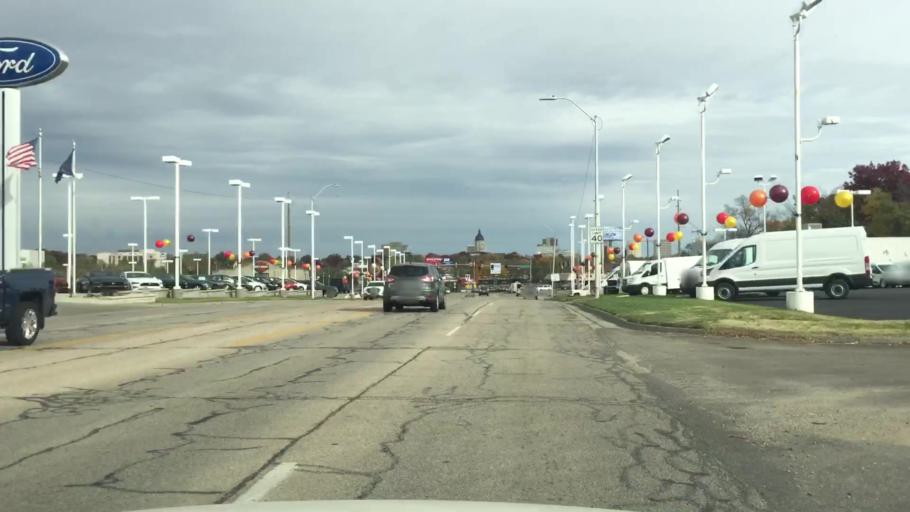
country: US
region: Kansas
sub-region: Shawnee County
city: Topeka
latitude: 39.0279
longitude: -95.6834
